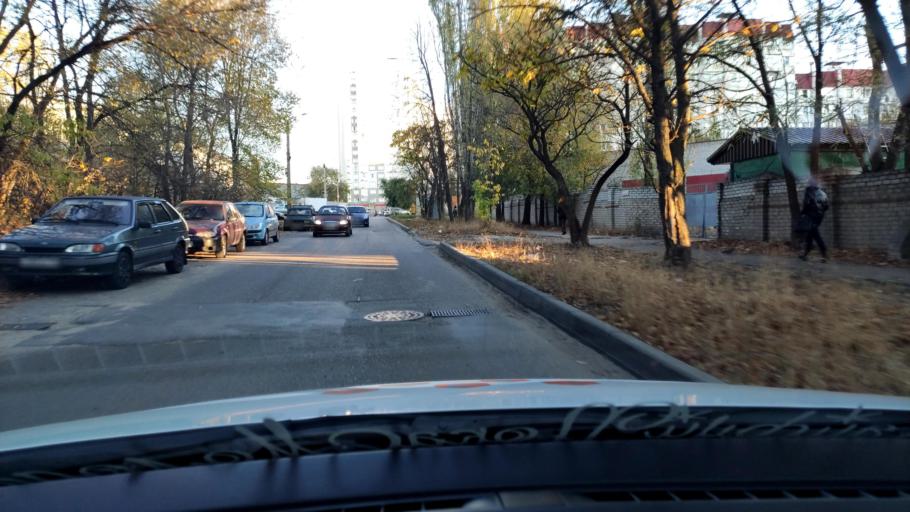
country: RU
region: Voronezj
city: Podgornoye
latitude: 51.6914
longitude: 39.1444
